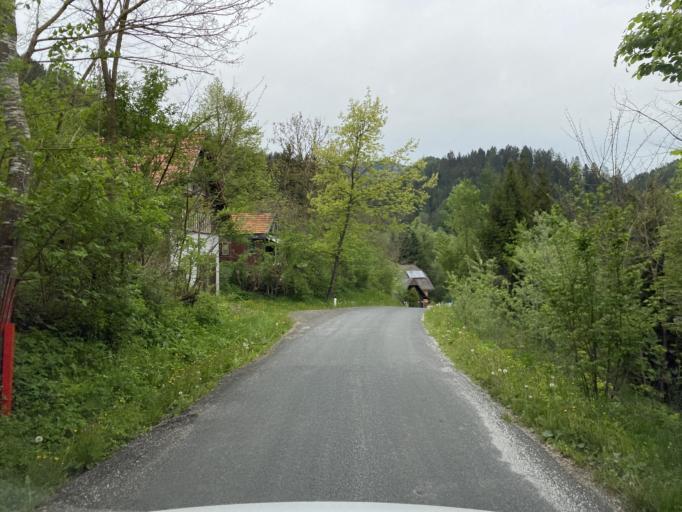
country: AT
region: Styria
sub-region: Politischer Bezirk Weiz
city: Koglhof
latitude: 47.3111
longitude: 15.6871
